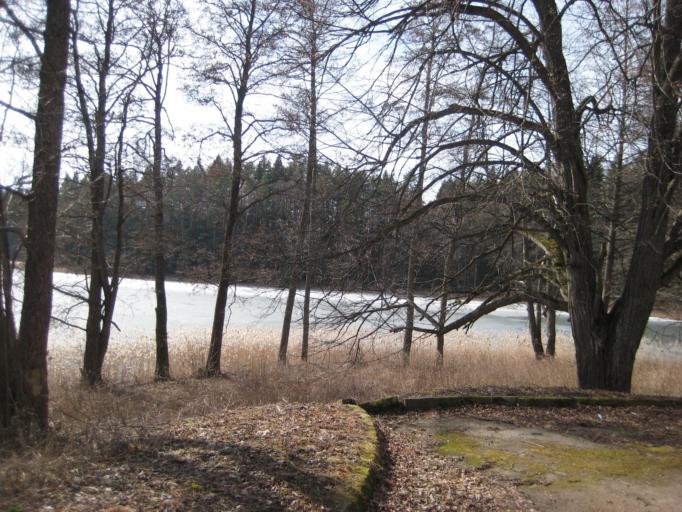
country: LT
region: Panevezys
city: Rokiskis
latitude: 55.8259
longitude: 25.8687
